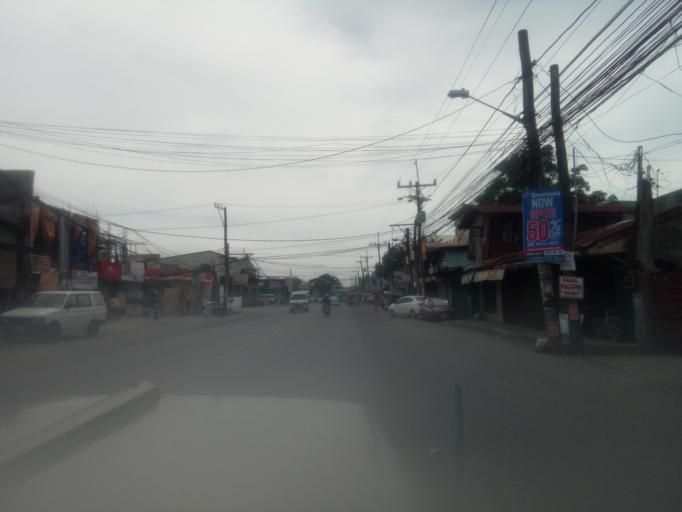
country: PH
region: Calabarzon
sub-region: Province of Cavite
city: Bulihan
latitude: 14.2867
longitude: 121.0011
